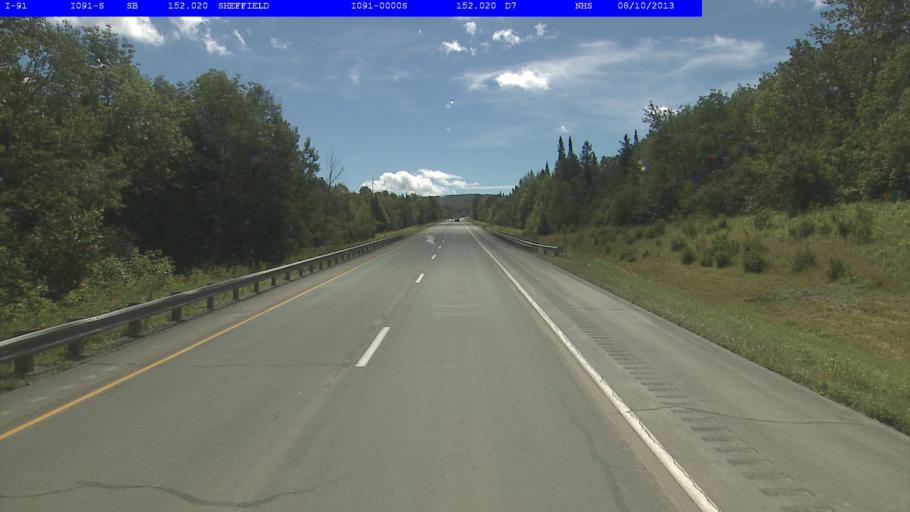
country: US
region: Vermont
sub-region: Caledonia County
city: Lyndonville
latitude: 44.6929
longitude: -72.1401
